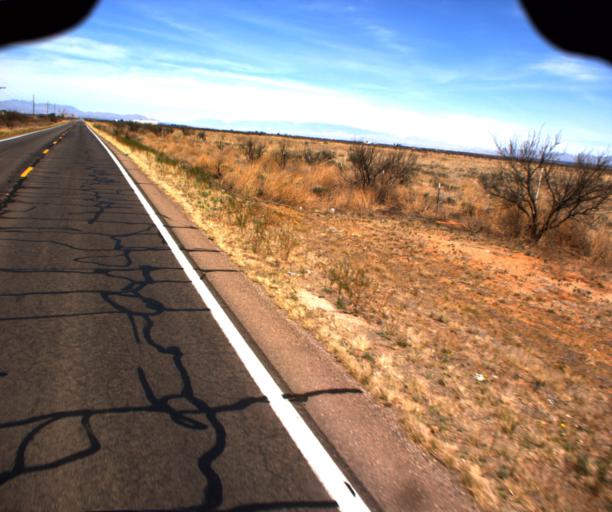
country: US
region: Arizona
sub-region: Cochise County
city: Willcox
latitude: 31.9874
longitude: -109.8545
